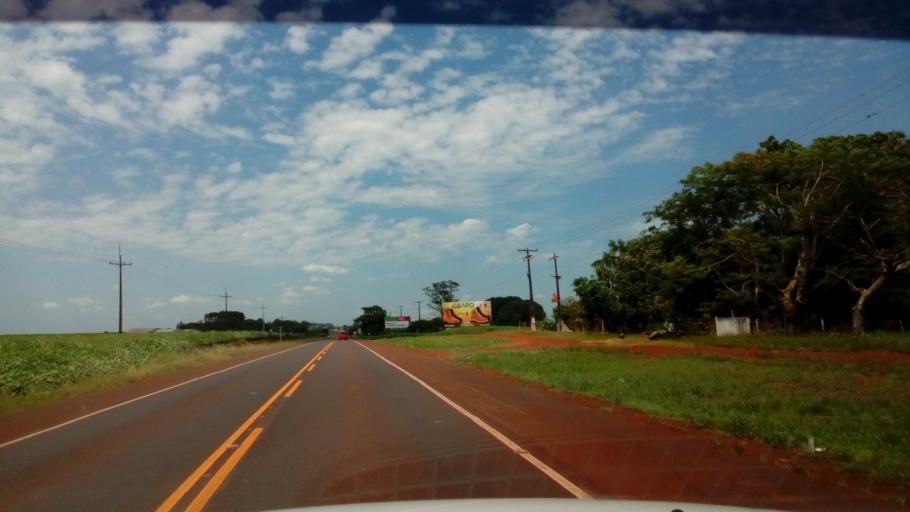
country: PY
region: Alto Parana
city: Santa Rita
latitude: -25.7310
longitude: -55.0423
